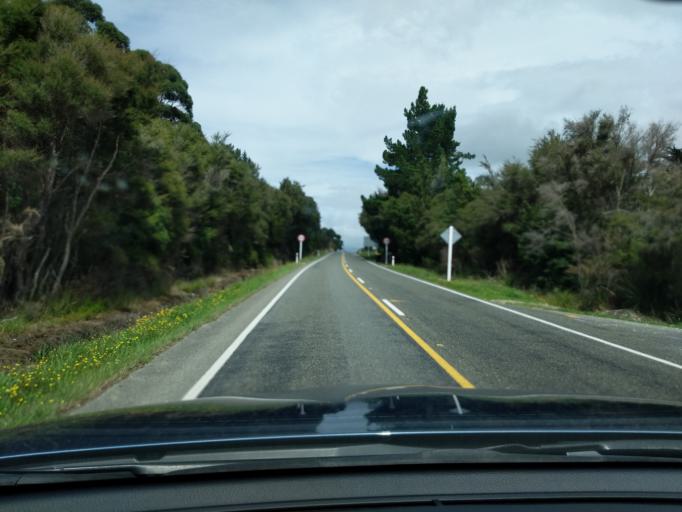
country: NZ
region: Tasman
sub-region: Tasman District
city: Takaka
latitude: -40.6829
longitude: 172.6736
